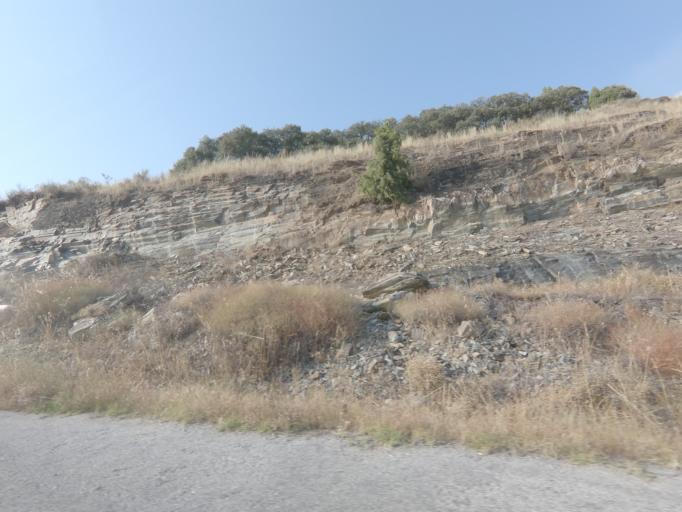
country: PT
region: Viseu
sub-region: Tabuaco
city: Tabuaco
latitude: 41.1300
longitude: -7.5435
